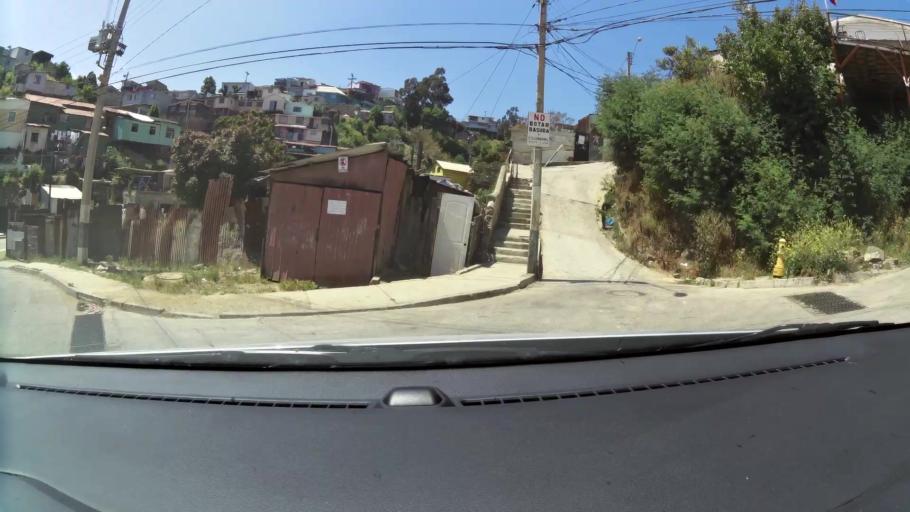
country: CL
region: Valparaiso
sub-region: Provincia de Valparaiso
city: Valparaiso
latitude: -33.0417
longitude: -71.6393
